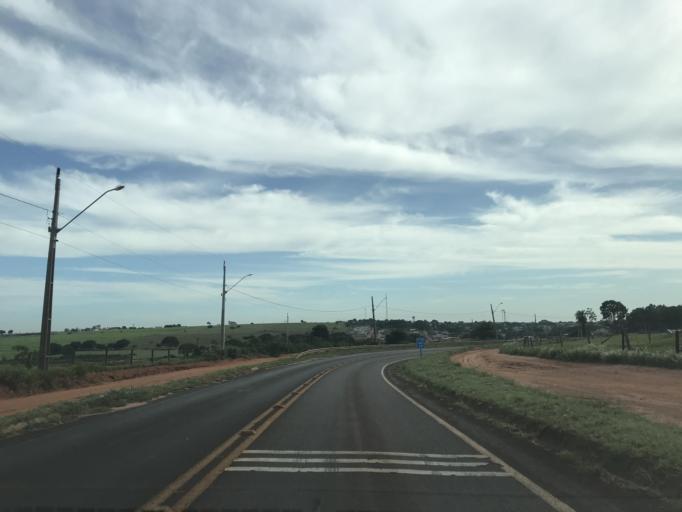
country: BR
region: Parana
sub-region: Paranavai
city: Nova Aurora
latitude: -22.9444
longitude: -52.6964
